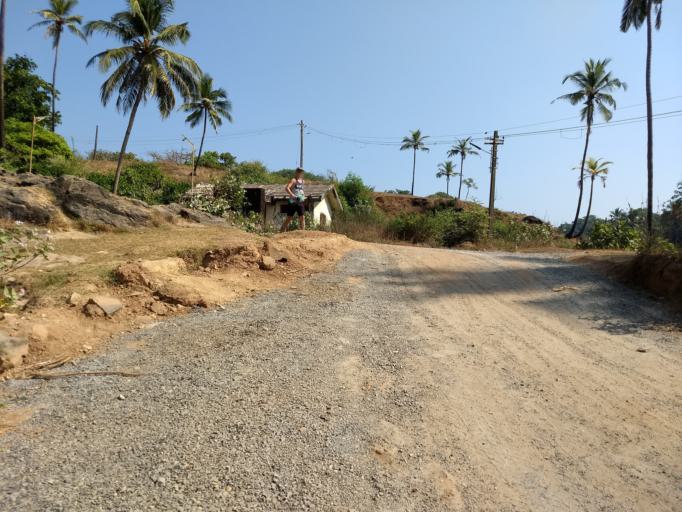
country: IN
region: Goa
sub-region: North Goa
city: Vagator
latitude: 15.5988
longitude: 73.7338
